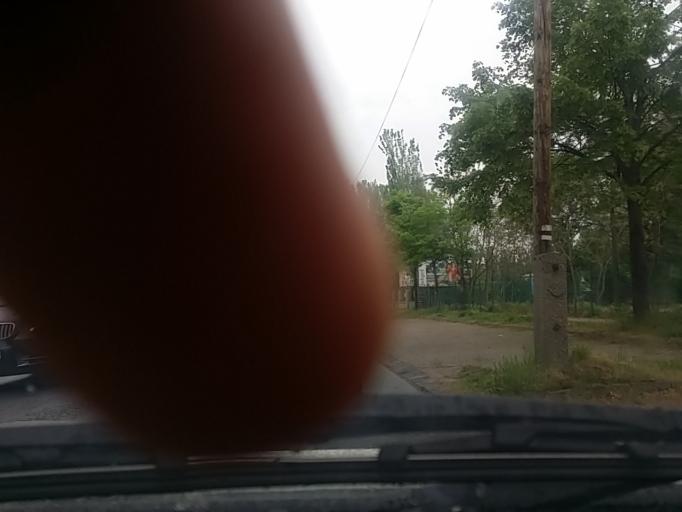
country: HU
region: Budapest
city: Budapest III. keruelet
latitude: 47.5401
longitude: 19.0624
